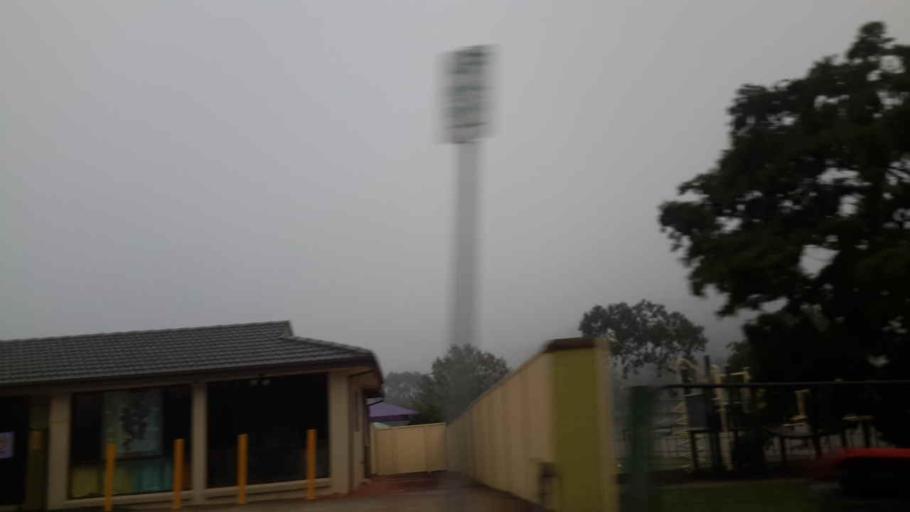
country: AU
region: New South Wales
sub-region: Wollondilly
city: Douglas Park
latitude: -34.1825
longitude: 150.7108
